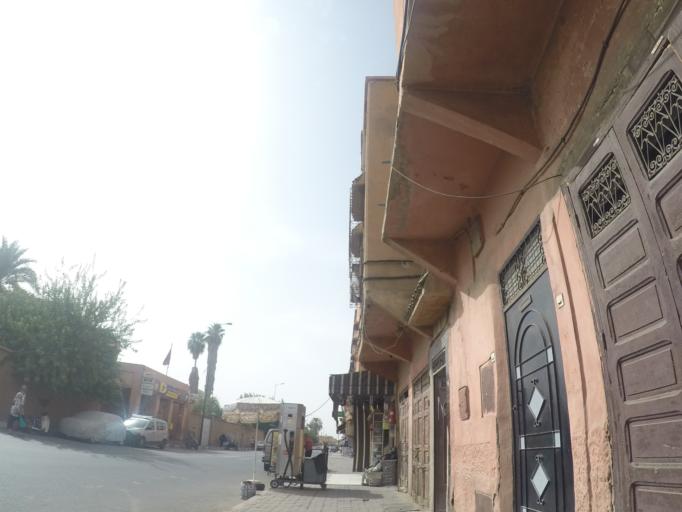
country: MA
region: Marrakech-Tensift-Al Haouz
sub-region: Marrakech
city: Marrakesh
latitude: 31.5998
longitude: -8.0215
